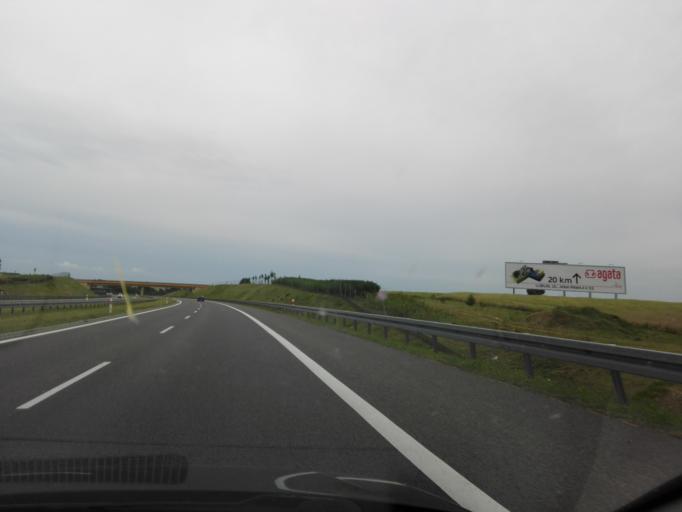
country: PL
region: Lublin Voivodeship
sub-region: Powiat lubelski
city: Jastkow
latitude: 51.3170
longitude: 22.3859
